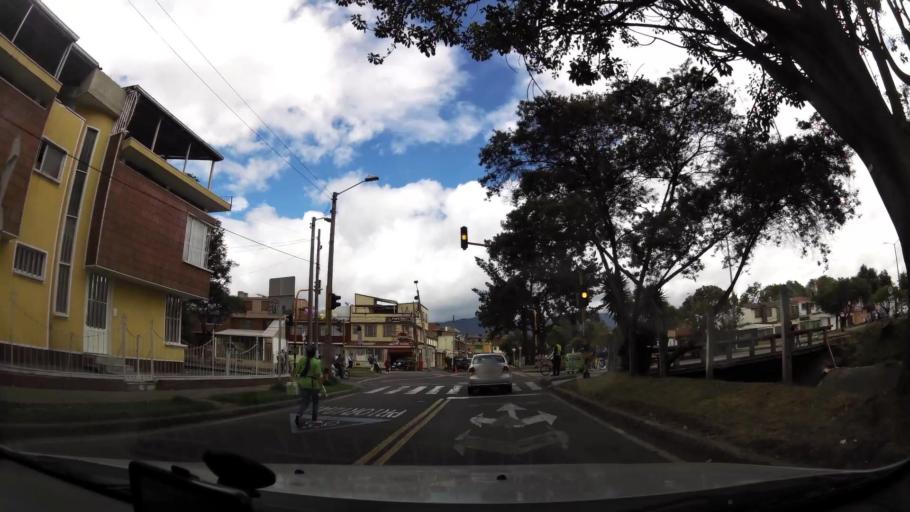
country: CO
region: Bogota D.C.
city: Bogota
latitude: 4.5979
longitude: -74.1254
